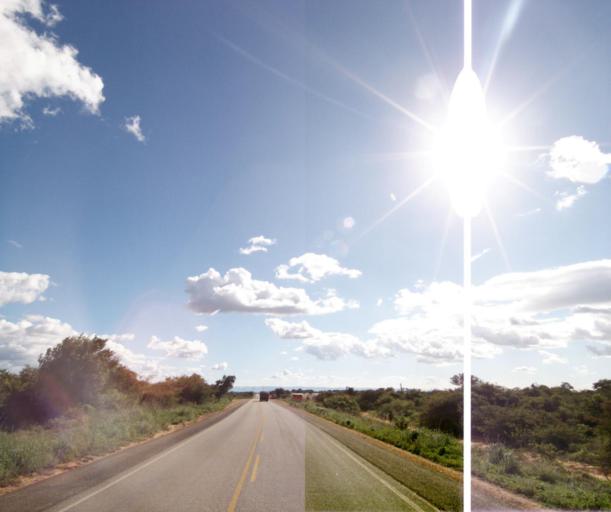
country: BR
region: Bahia
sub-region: Guanambi
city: Guanambi
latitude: -14.1343
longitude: -42.6355
